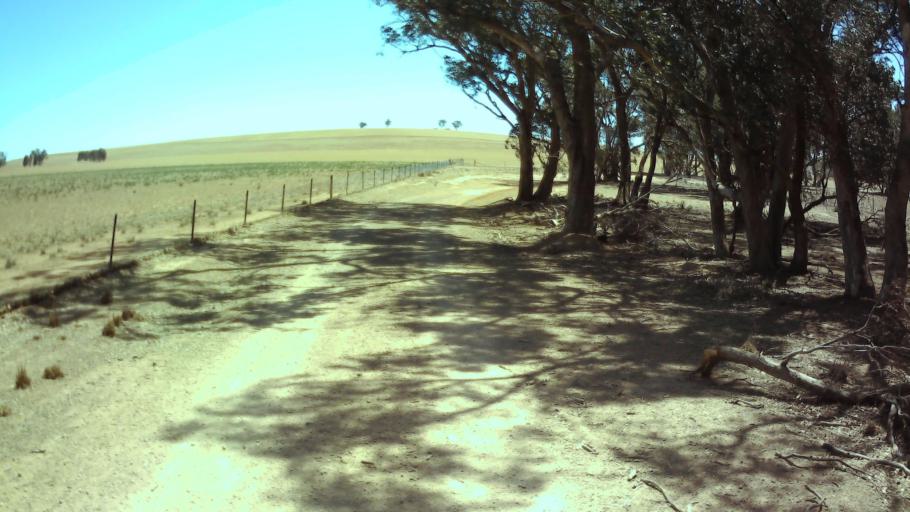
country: AU
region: New South Wales
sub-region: Weddin
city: Grenfell
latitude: -33.9819
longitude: 148.1655
